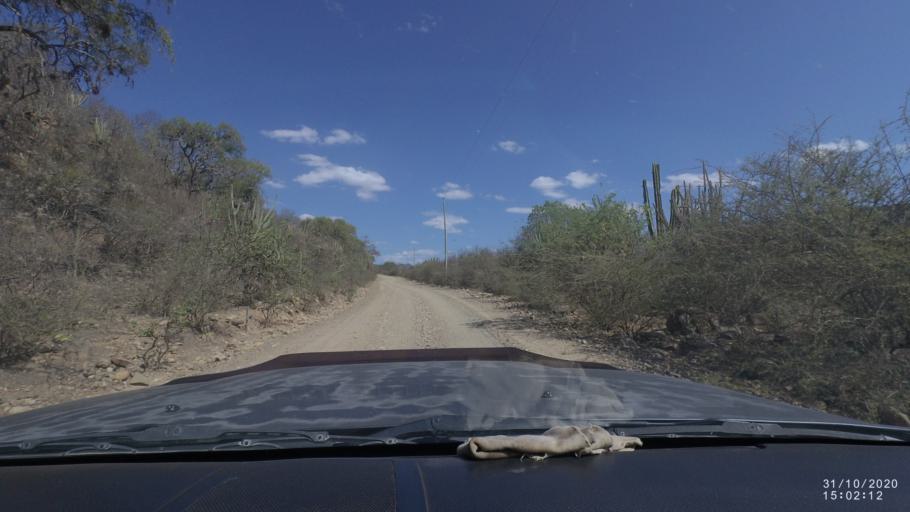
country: BO
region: Cochabamba
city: Aiquile
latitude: -18.2684
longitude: -64.8140
